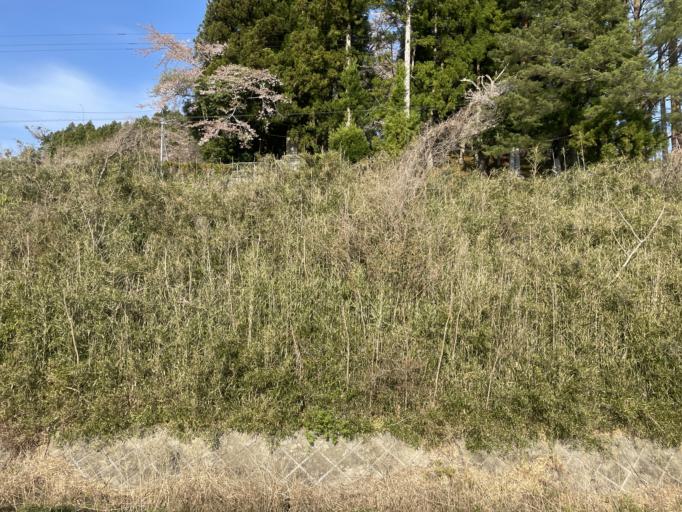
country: JP
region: Iwate
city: Ofunato
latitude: 39.1164
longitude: 141.8100
